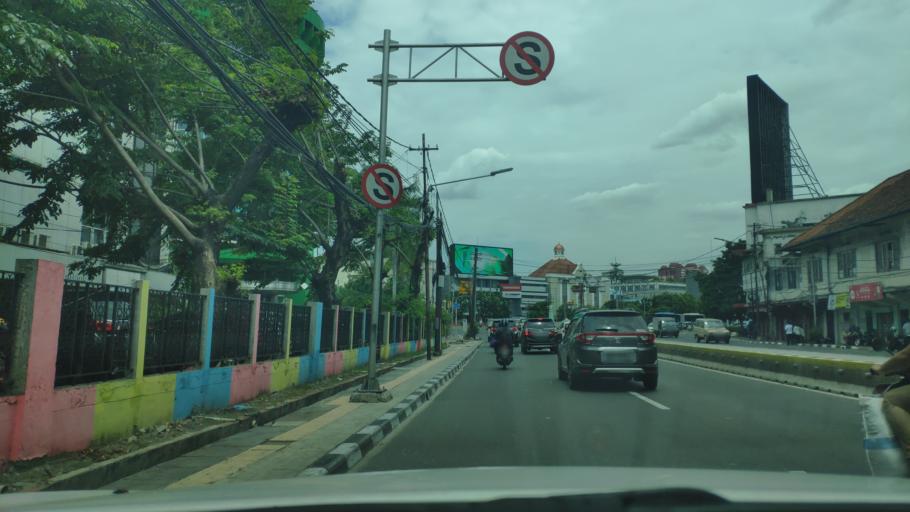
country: ID
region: Jakarta Raya
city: Jakarta
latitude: -6.1684
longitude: 106.8200
